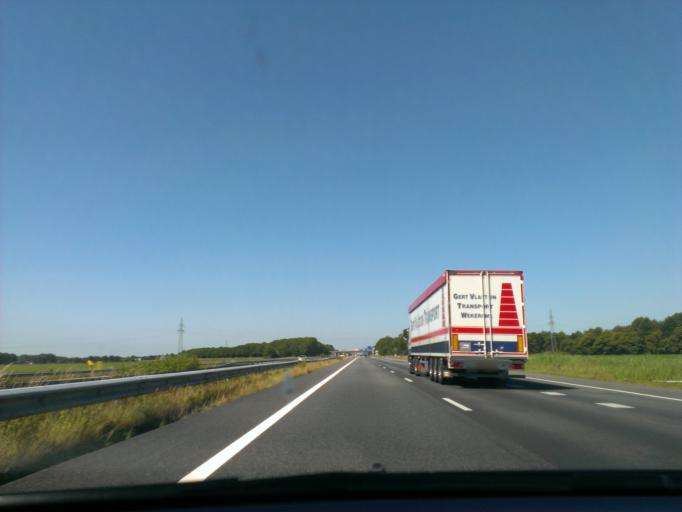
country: NL
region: Drenthe
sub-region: Gemeente Hoogeveen
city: Hoogeveen
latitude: 52.7086
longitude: 6.4689
